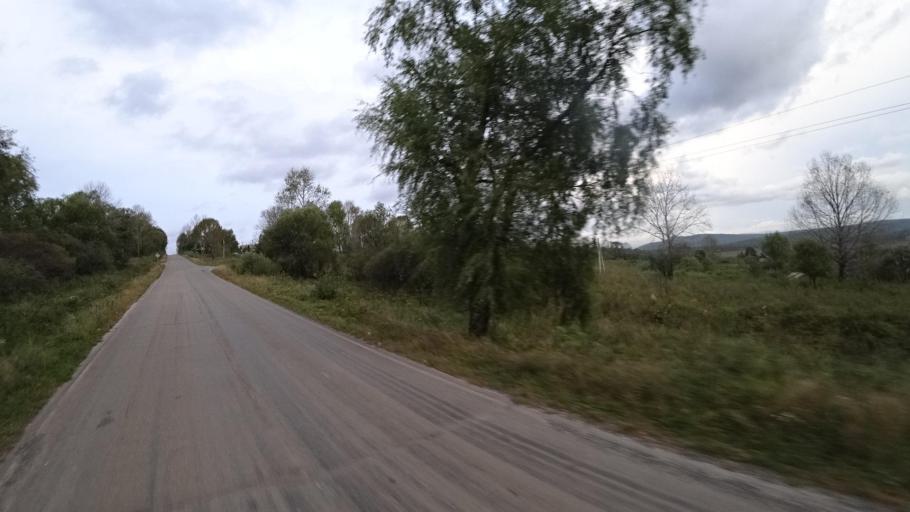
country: RU
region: Jewish Autonomous Oblast
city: Izvestkovyy
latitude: 48.9741
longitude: 131.5774
